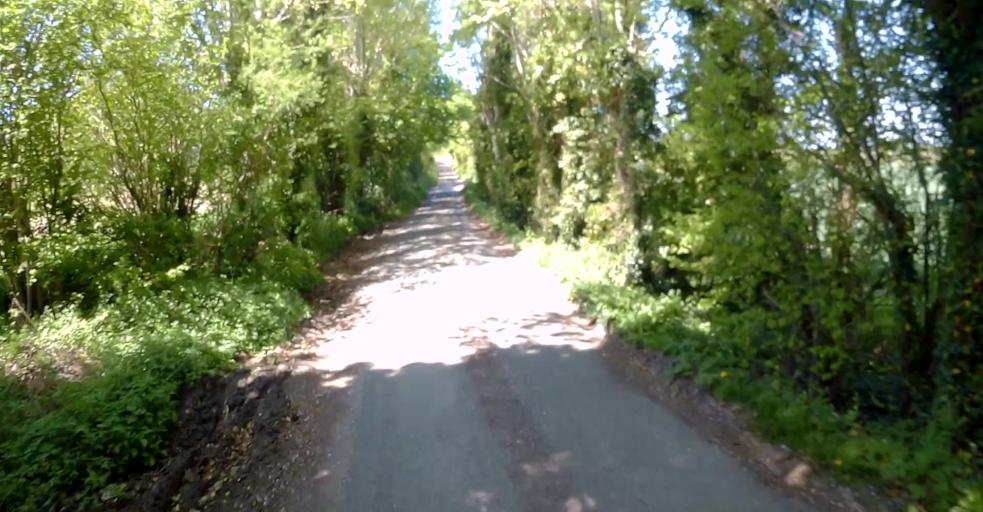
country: GB
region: England
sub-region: Hampshire
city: Overton
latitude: 51.2154
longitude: -1.3139
